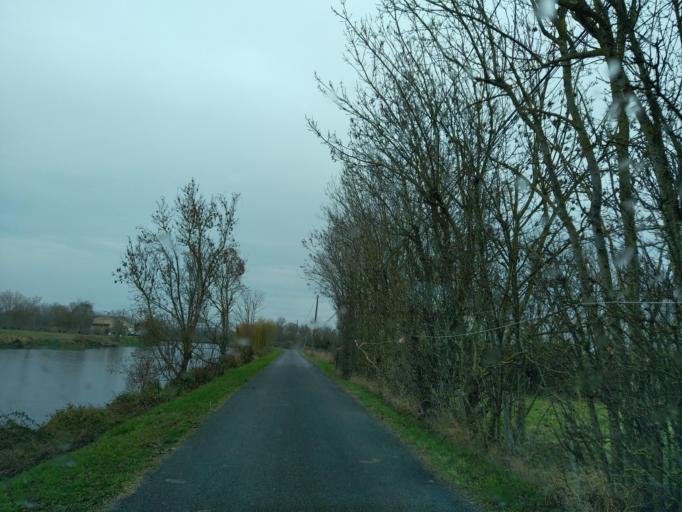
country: FR
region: Pays de la Loire
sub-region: Departement de la Vendee
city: Maillezais
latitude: 46.3186
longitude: -0.7802
